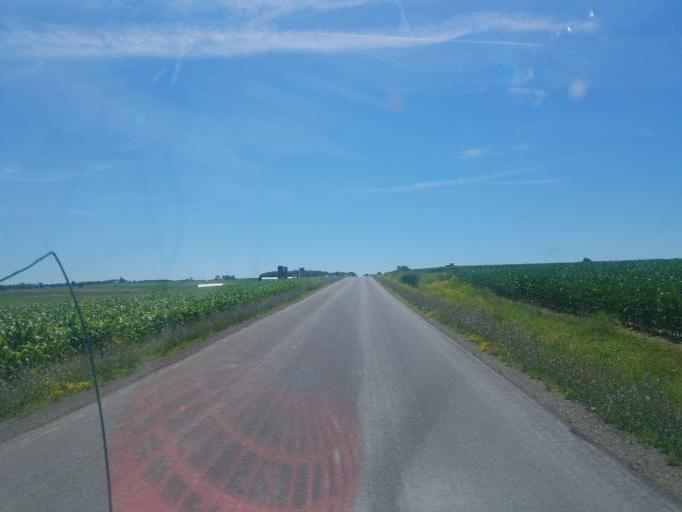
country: US
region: New York
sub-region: Yates County
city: Penn Yan
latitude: 42.6494
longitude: -77.0177
